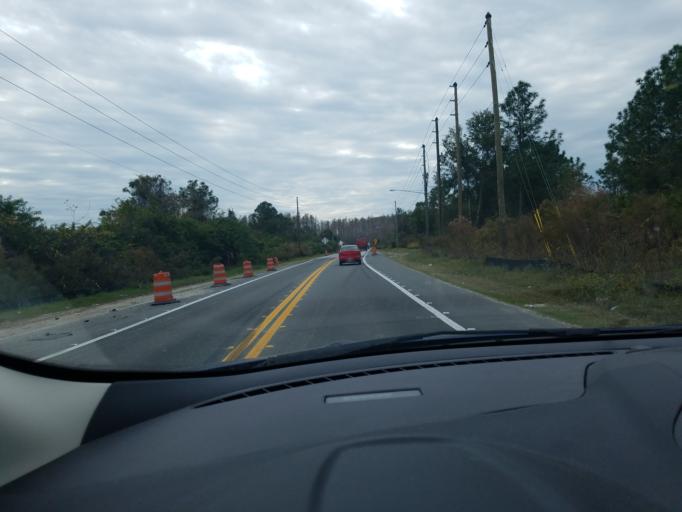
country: US
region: Florida
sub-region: Orange County
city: Hunters Creek
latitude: 28.3564
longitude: -81.3896
